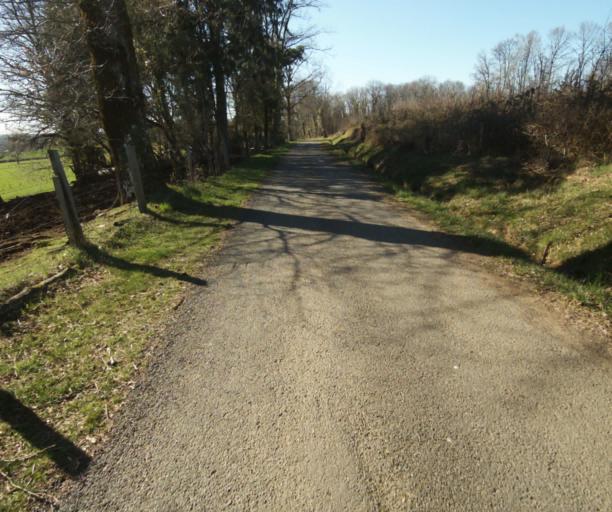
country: FR
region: Limousin
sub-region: Departement de la Correze
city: Chamboulive
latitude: 45.3960
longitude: 1.6805
